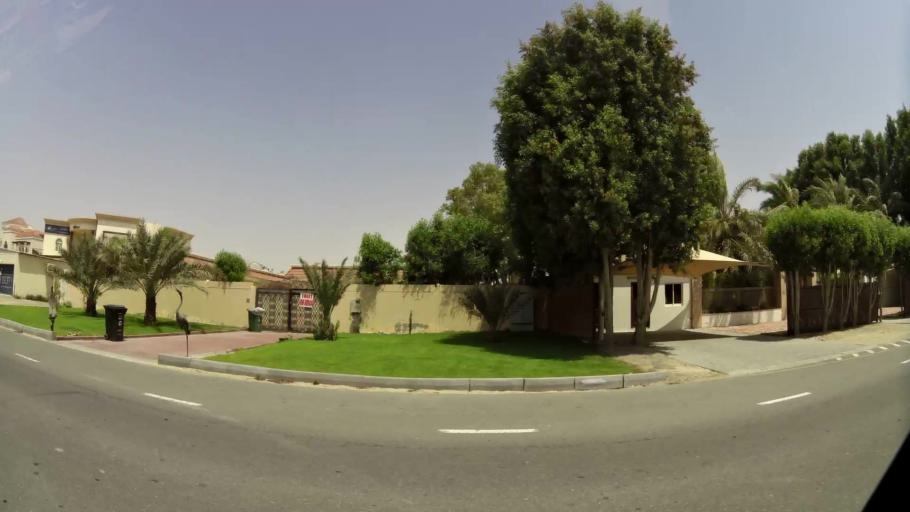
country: AE
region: Dubai
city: Dubai
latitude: 25.1318
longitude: 55.2052
